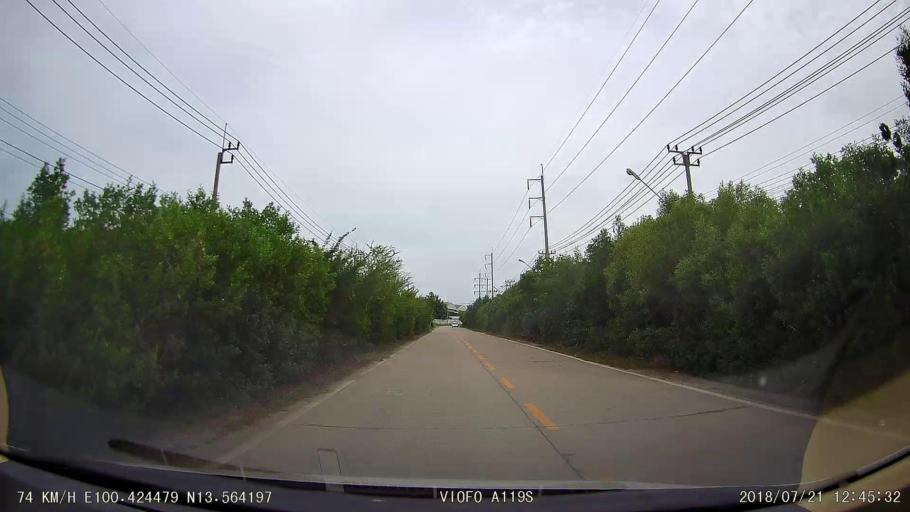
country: TH
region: Bangkok
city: Bang Khun Thian
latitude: 13.5639
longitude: 100.4240
